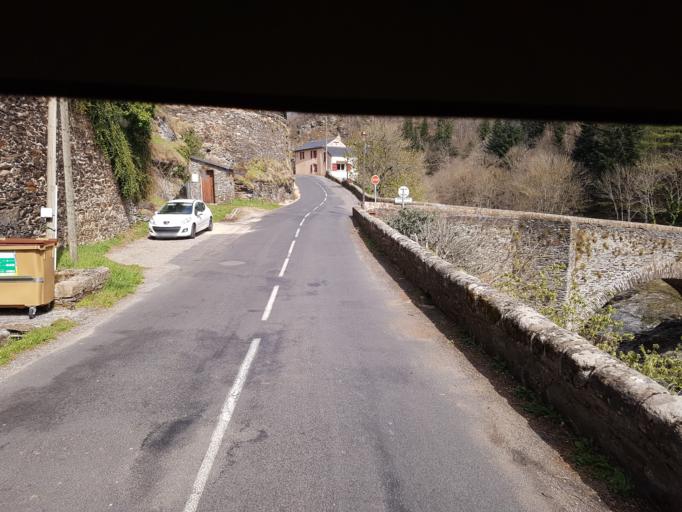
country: FR
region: Languedoc-Roussillon
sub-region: Departement de la Lozere
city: Florac
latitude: 44.2386
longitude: 3.5781
